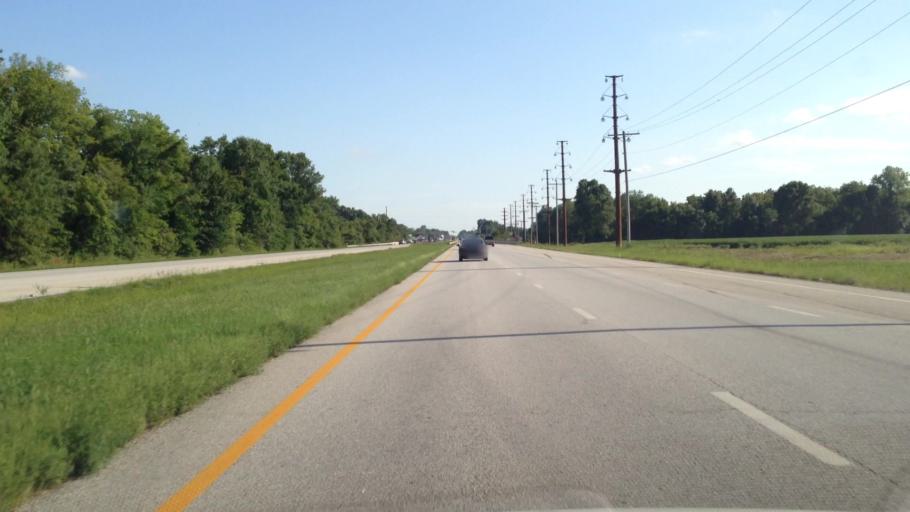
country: US
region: Kansas
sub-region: Crawford County
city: Frontenac
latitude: 37.4765
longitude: -94.7053
